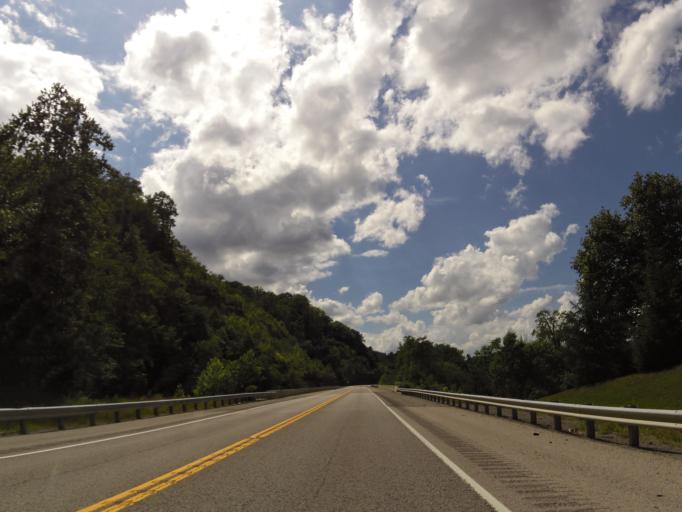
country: US
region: Kentucky
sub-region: Harlan County
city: Harlan
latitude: 36.7834
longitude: -83.2423
